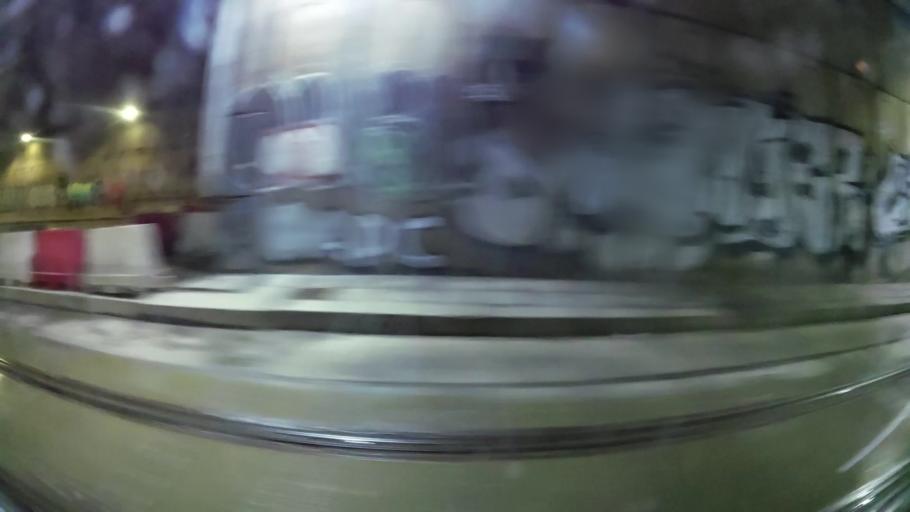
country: BG
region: Sofia-Capital
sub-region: Stolichna Obshtina
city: Sofia
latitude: 42.6851
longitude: 23.3205
